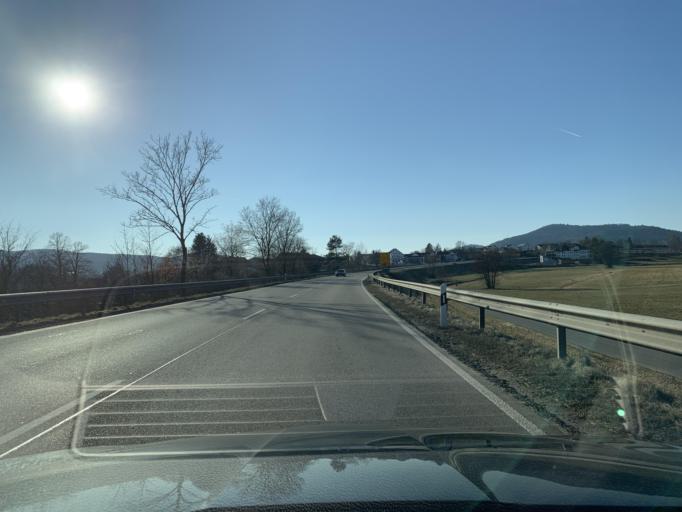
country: DE
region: Bavaria
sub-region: Upper Palatinate
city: Roetz
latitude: 49.3425
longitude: 12.5441
